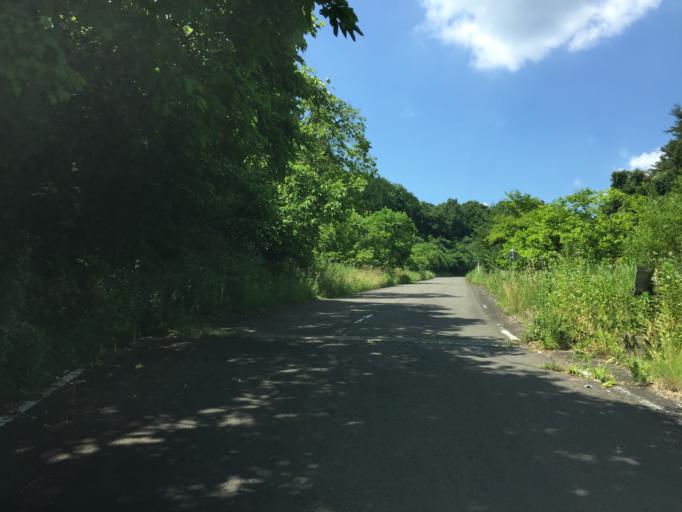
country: JP
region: Fukushima
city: Yanagawamachi-saiwaicho
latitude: 37.7735
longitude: 140.6536
